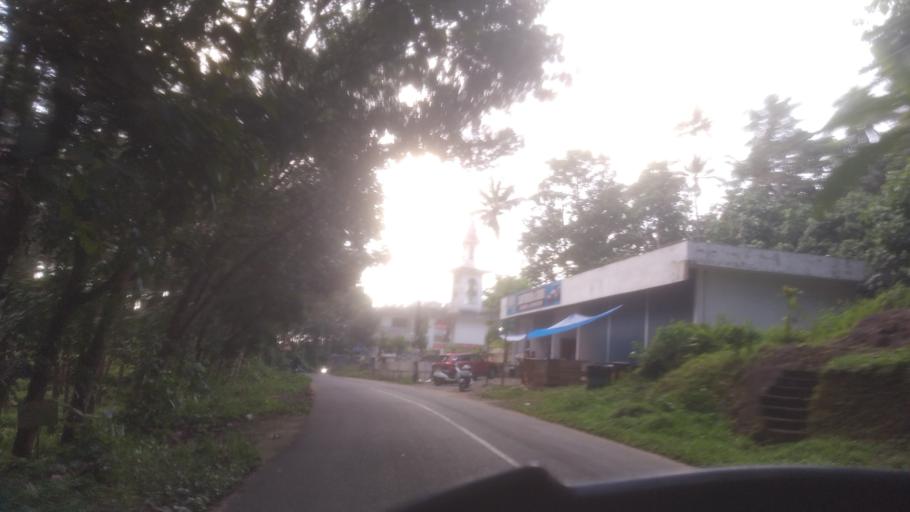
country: IN
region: Kerala
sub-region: Ernakulam
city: Kotamangalam
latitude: 10.0050
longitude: 76.6681
